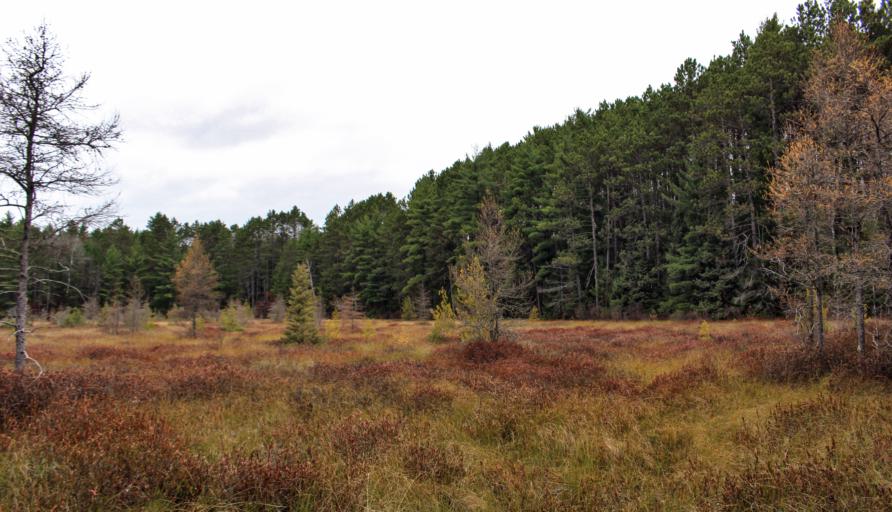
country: US
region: Wisconsin
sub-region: Vilas County
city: Eagle River
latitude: 45.8763
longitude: -89.0314
